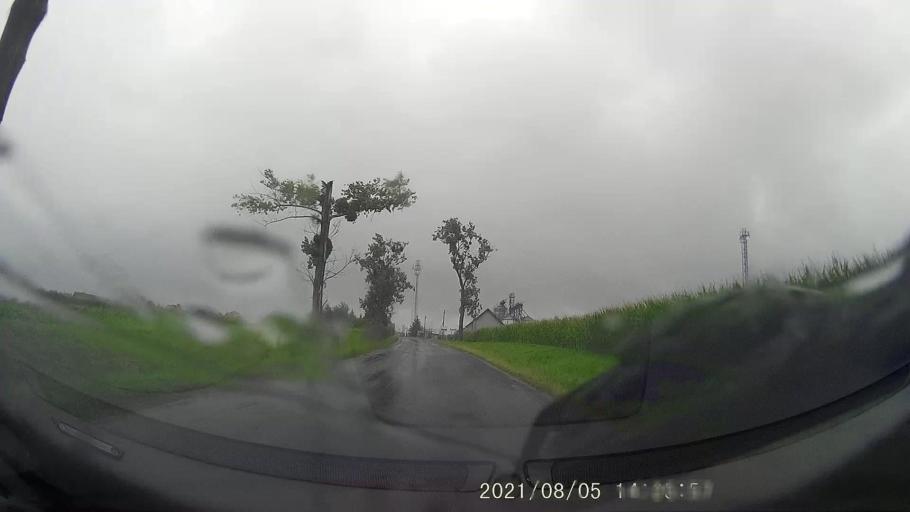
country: PL
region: Opole Voivodeship
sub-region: Powiat nyski
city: Korfantow
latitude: 50.4858
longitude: 17.6084
